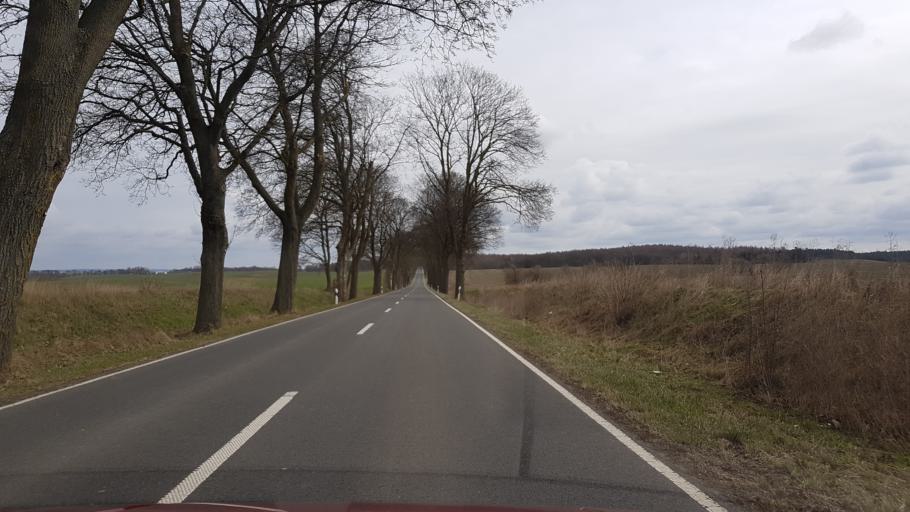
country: DE
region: Brandenburg
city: Mescherin
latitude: 53.2654
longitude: 14.4065
